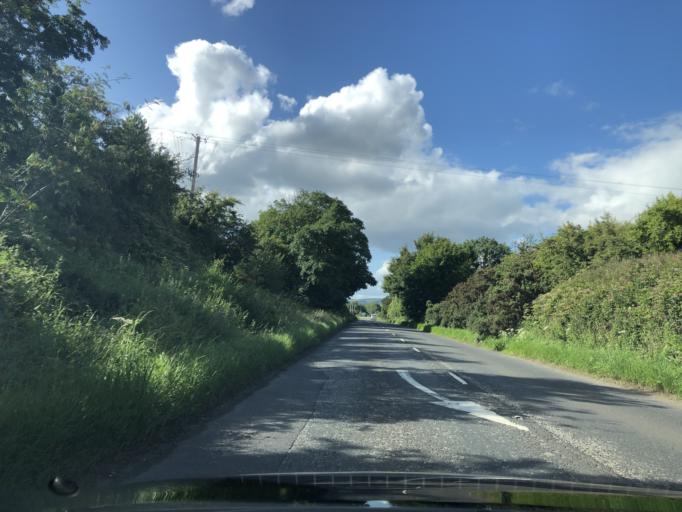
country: GB
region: Northern Ireland
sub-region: Ards District
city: Comber
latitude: 54.5552
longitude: -5.7570
